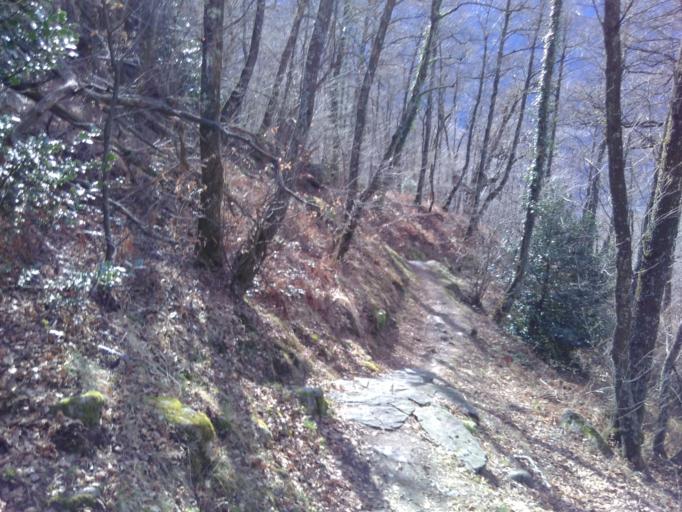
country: CH
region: Ticino
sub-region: Locarno District
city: Verscio
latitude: 46.2513
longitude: 8.7139
